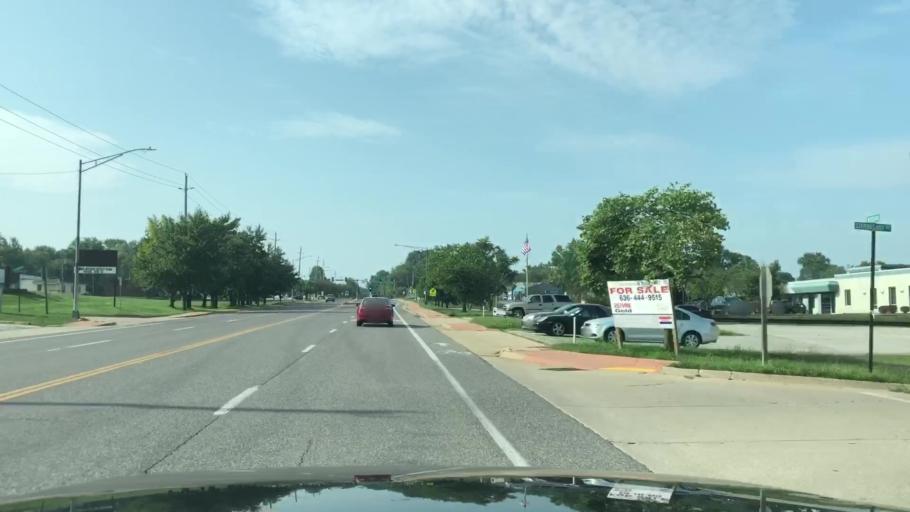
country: US
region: Missouri
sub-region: Saint Louis County
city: Woodson Terrace
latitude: 38.7297
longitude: -90.3577
